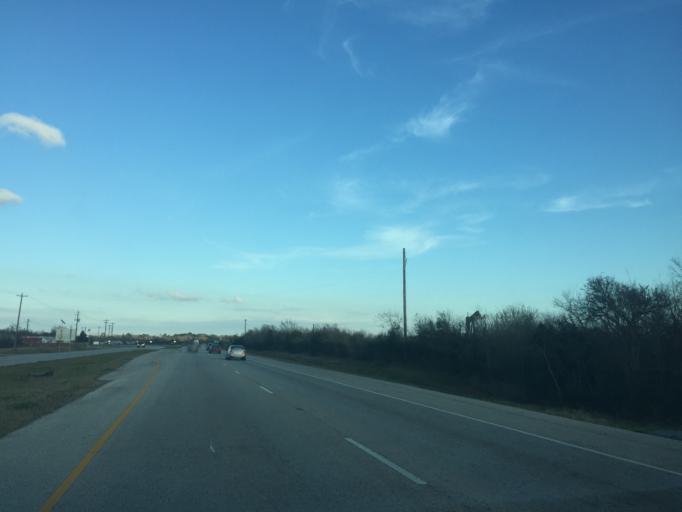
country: US
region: Texas
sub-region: Harris County
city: Baytown
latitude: 29.7135
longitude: -94.9880
